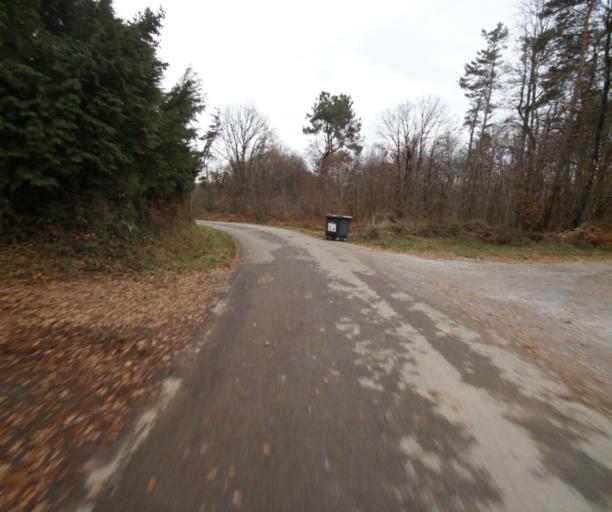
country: FR
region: Limousin
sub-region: Departement de la Correze
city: Cornil
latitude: 45.2322
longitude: 1.6533
